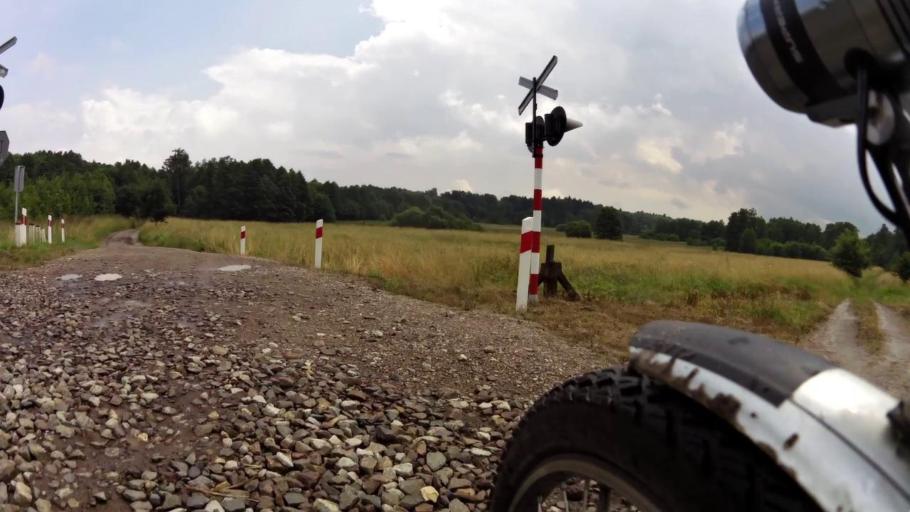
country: PL
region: West Pomeranian Voivodeship
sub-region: Powiat lobeski
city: Lobez
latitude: 53.7278
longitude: 15.6775
